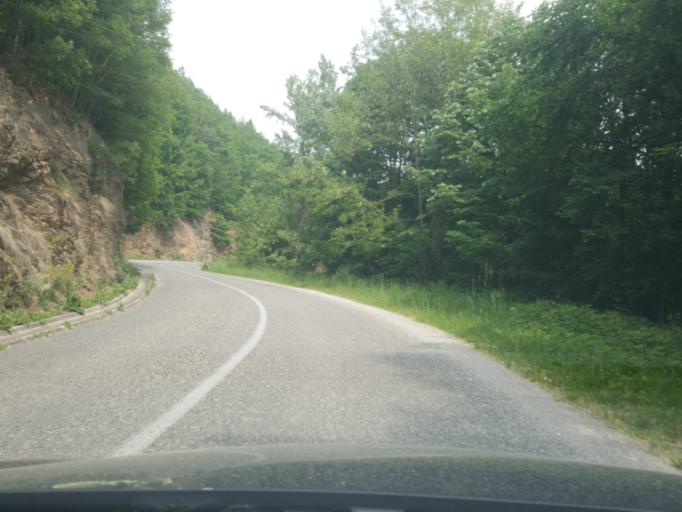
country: RS
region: Central Serbia
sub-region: Zlatiborski Okrug
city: Bajina Basta
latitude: 44.0423
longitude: 19.6258
